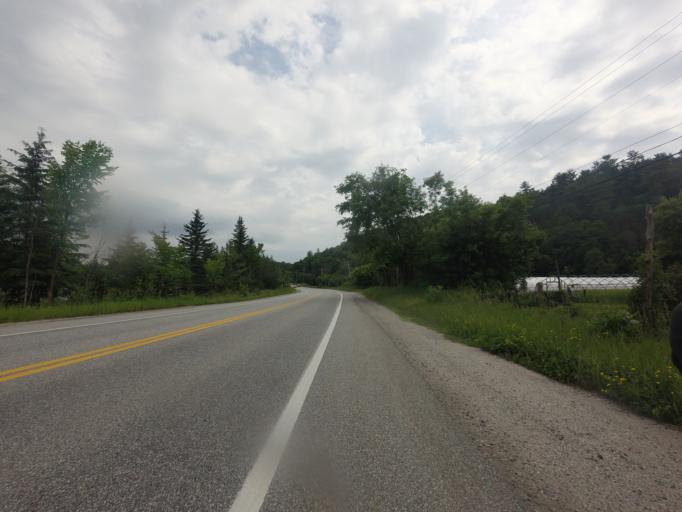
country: CA
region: Quebec
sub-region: Outaouais
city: Wakefield
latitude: 45.6901
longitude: -75.9321
